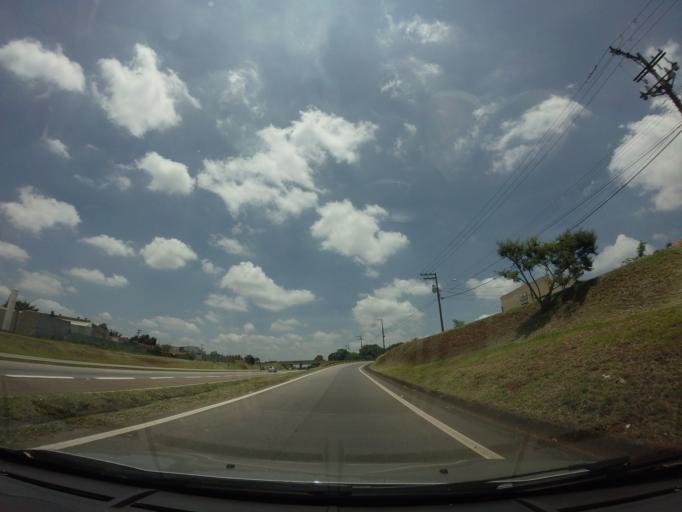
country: BR
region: Sao Paulo
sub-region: Piracicaba
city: Piracicaba
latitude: -22.7617
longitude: -47.5963
